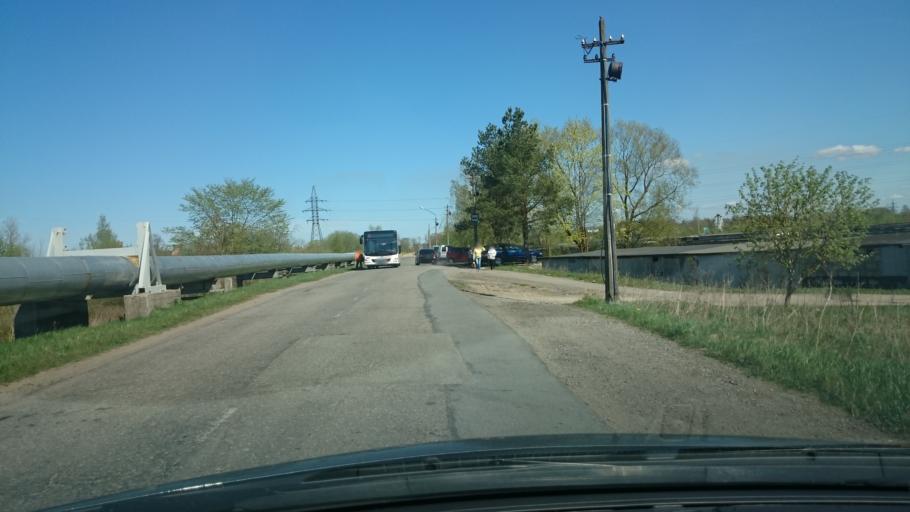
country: EE
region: Ida-Virumaa
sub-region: Narva linn
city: Narva
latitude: 59.3520
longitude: 28.1770
